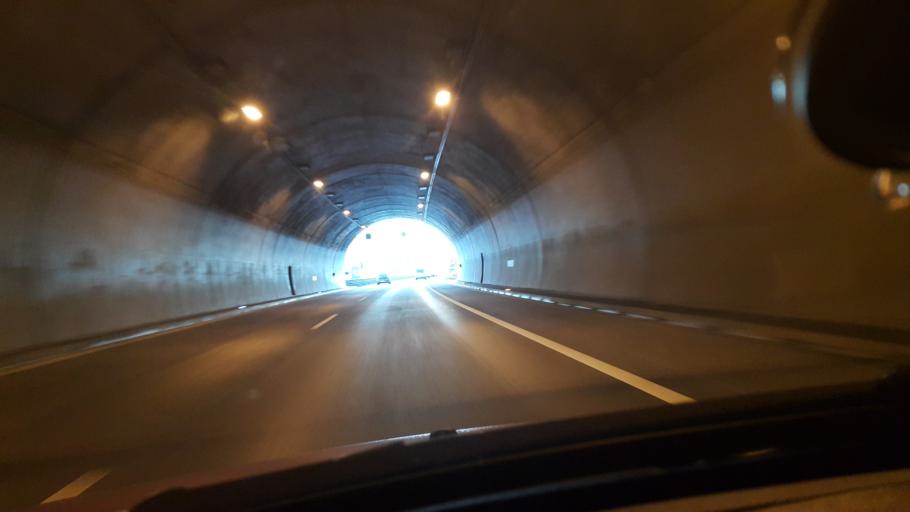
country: SI
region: Maribor
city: Maribor
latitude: 46.5663
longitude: 15.6858
